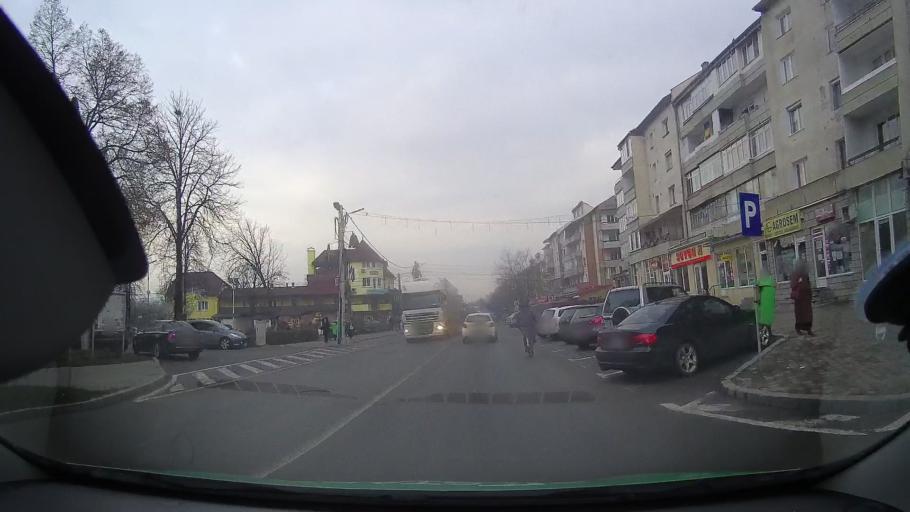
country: RO
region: Mures
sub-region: Comuna Ludus
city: Ludus
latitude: 46.4748
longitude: 24.0955
